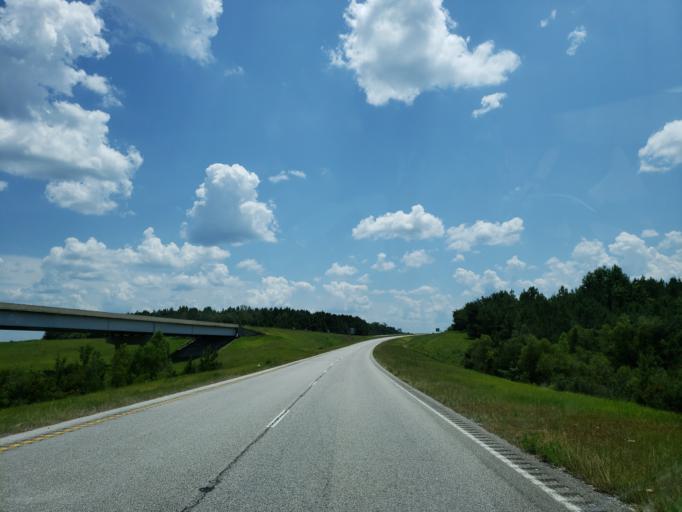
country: US
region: Mississippi
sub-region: Wayne County
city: Belmont
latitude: 31.4531
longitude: -88.4654
